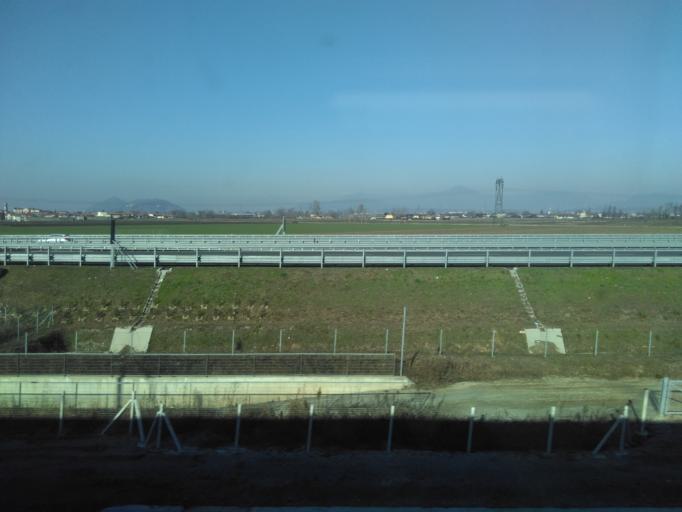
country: IT
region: Lombardy
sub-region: Provincia di Brescia
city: Duomo
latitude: 45.5256
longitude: 10.0330
